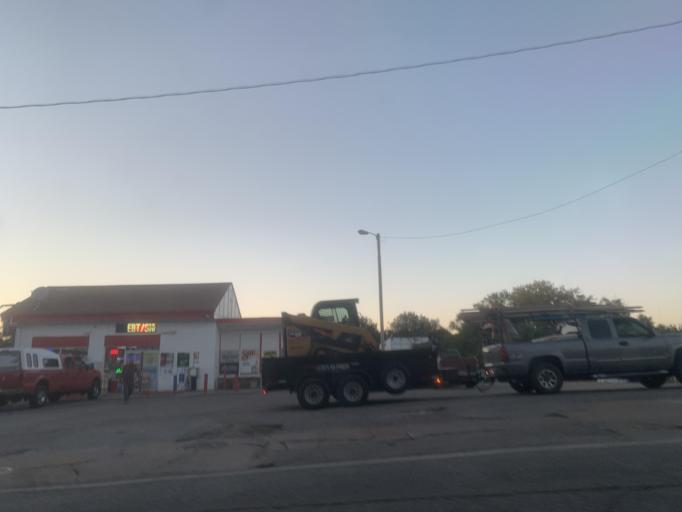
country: US
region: Nebraska
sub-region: Sarpy County
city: La Vista
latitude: 41.2053
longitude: -95.9881
